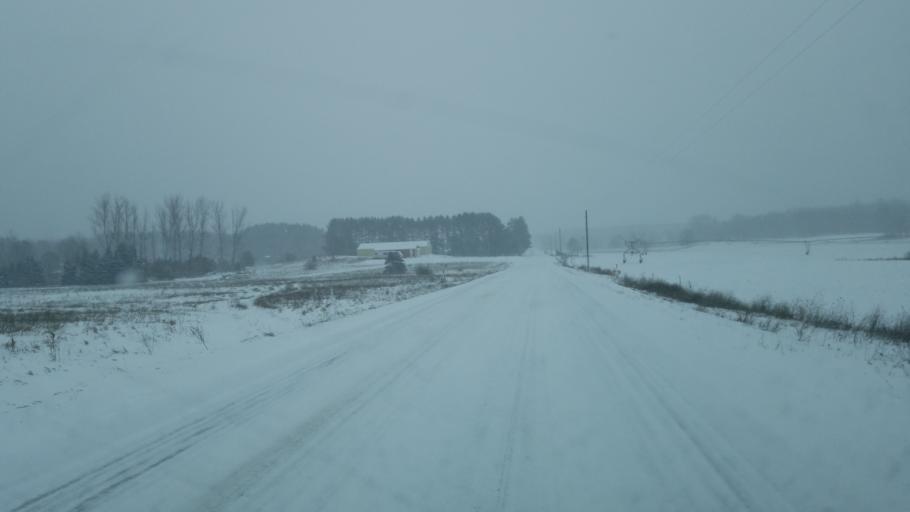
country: US
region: Michigan
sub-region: Mecosta County
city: Canadian Lakes
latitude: 43.5906
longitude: -85.3426
